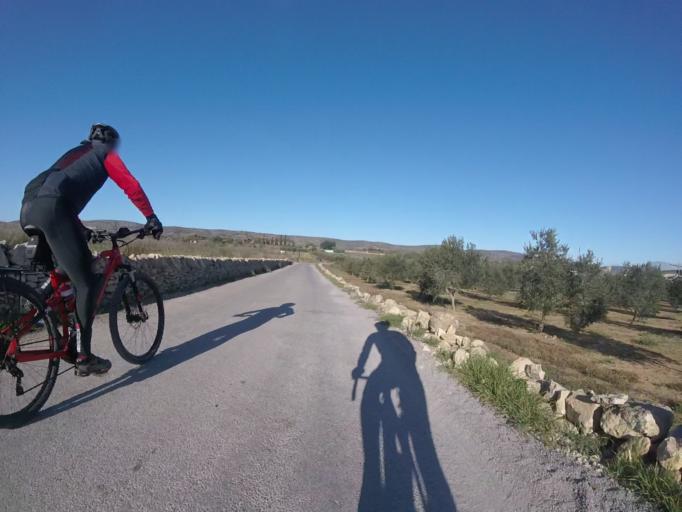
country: ES
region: Valencia
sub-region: Provincia de Castello
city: Alcala de Xivert
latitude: 40.2968
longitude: 0.2196
